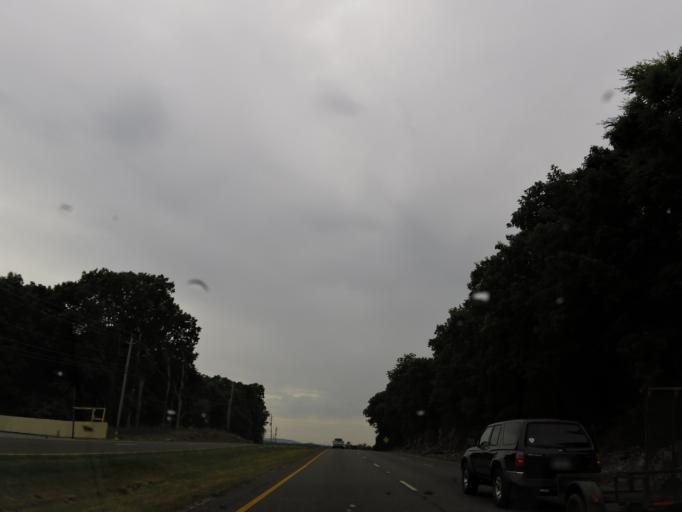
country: US
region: Alabama
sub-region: Madison County
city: Moores Mill
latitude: 34.7689
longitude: -86.4934
